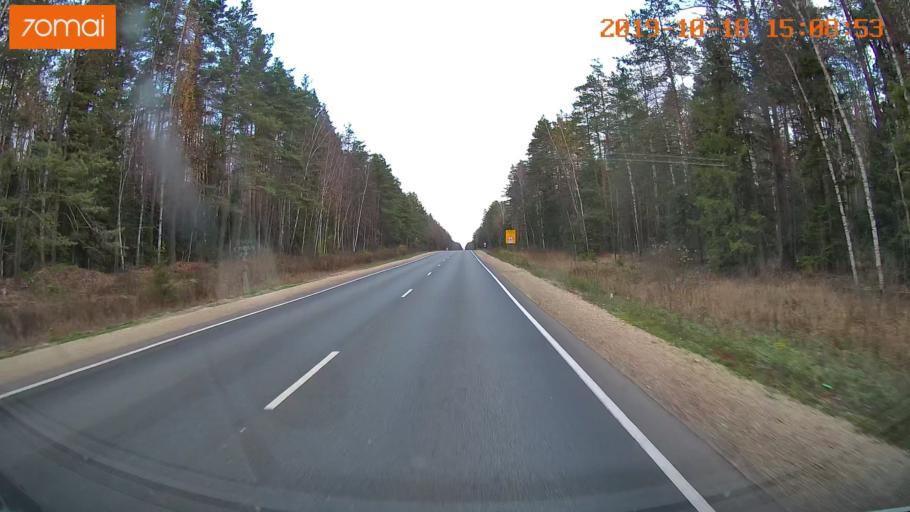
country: RU
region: Vladimir
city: Gus'-Khrustal'nyy
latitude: 55.5585
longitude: 40.6152
